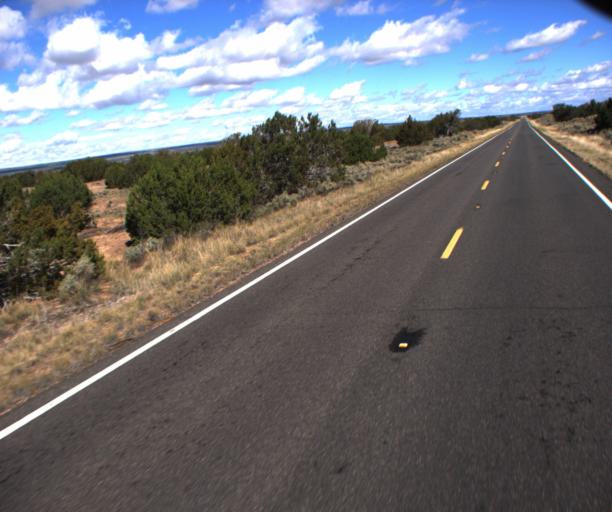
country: US
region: Arizona
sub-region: Apache County
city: Saint Johns
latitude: 34.8737
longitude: -109.2378
